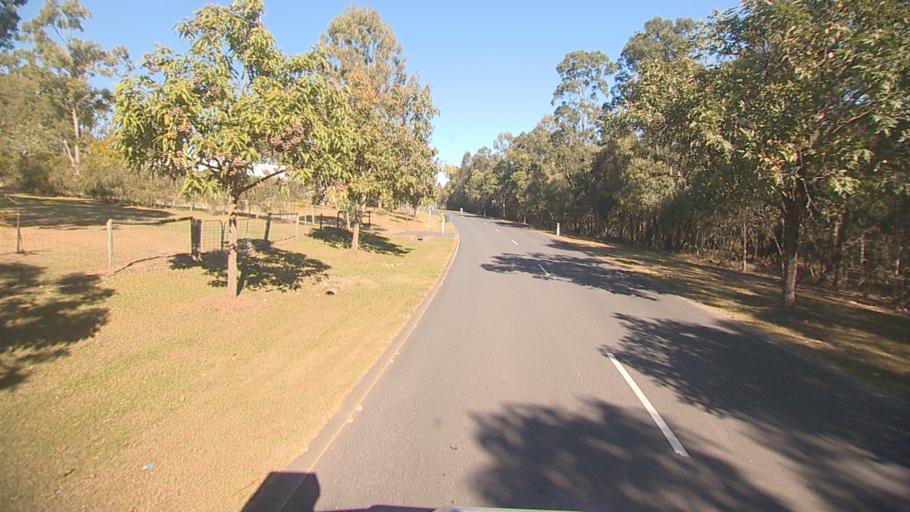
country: AU
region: Queensland
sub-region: Logan
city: North Maclean
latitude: -27.7530
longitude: 152.9554
